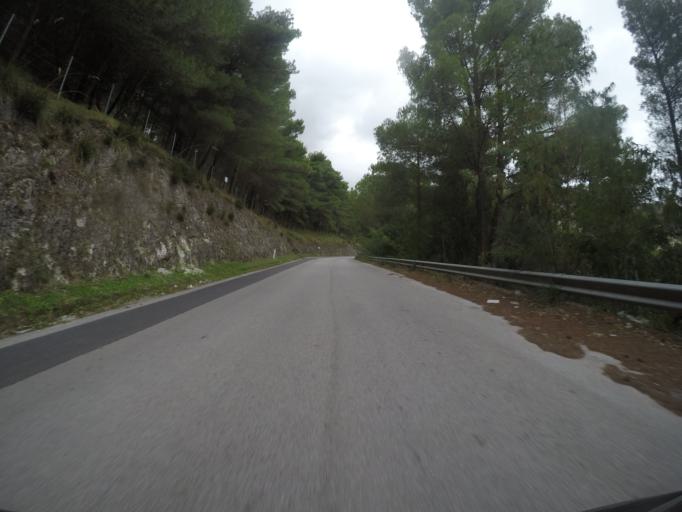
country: IT
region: Sicily
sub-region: Palermo
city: Montelepre
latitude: 38.1159
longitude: 13.1687
